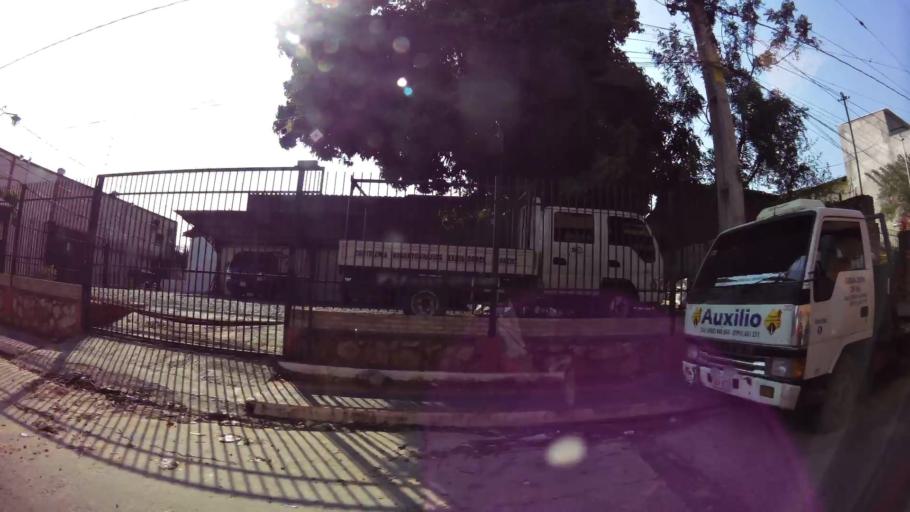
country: PY
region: Asuncion
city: Asuncion
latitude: -25.3093
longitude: -57.6241
